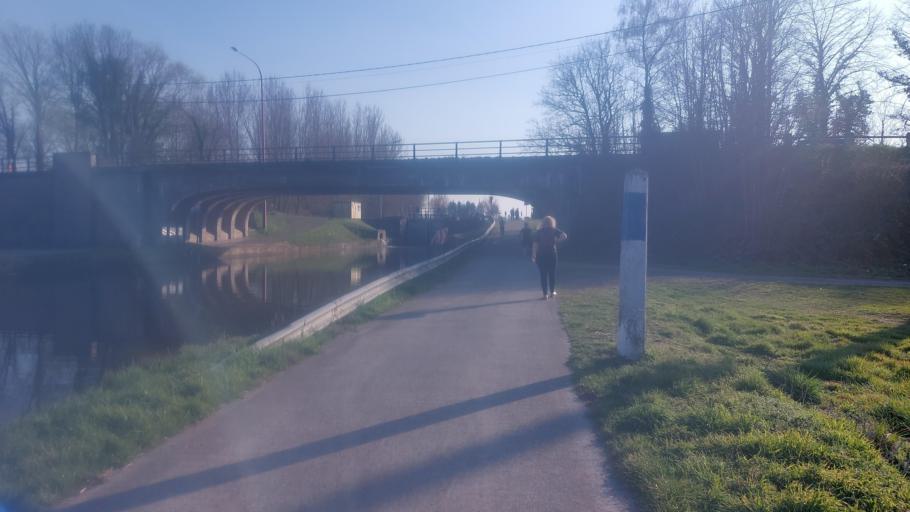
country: BE
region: Wallonia
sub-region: Province du Hainaut
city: Ath
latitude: 50.6154
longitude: 3.7924
